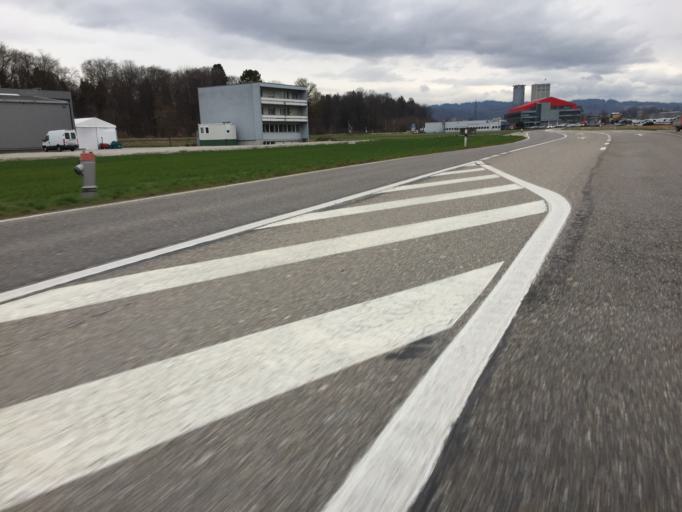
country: CH
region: Bern
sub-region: Emmental District
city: Lyssach
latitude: 47.0731
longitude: 7.5894
